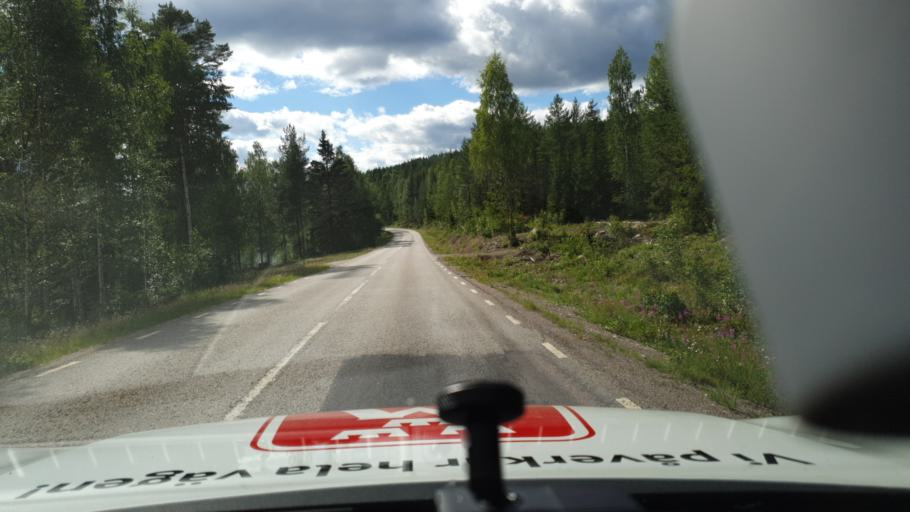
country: NO
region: Hedmark
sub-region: Trysil
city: Innbygda
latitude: 61.0297
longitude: 12.5742
